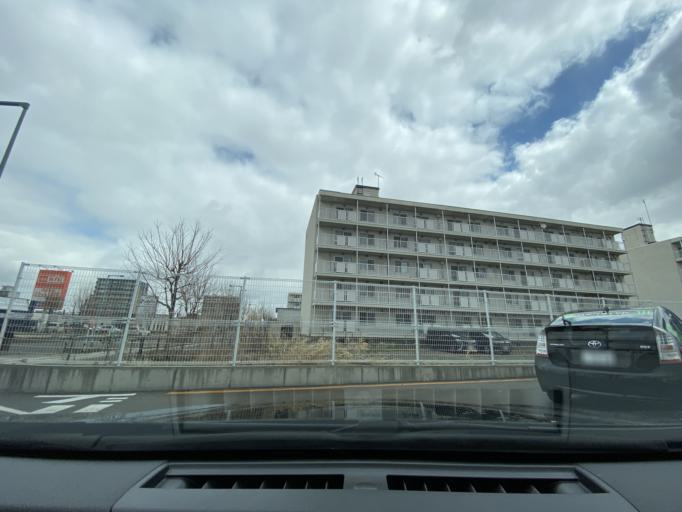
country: JP
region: Hokkaido
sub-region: Asahikawa-shi
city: Asahikawa
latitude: 43.7580
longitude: 142.3746
